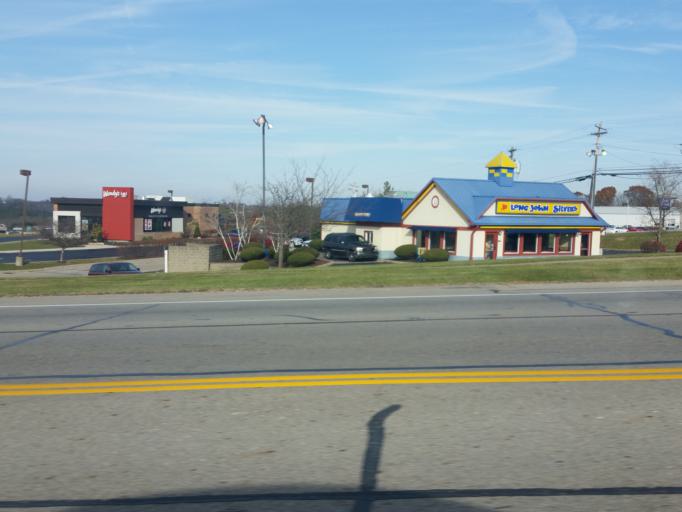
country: US
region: Kentucky
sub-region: Campbell County
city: Alexandria
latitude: 38.9825
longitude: -84.3986
